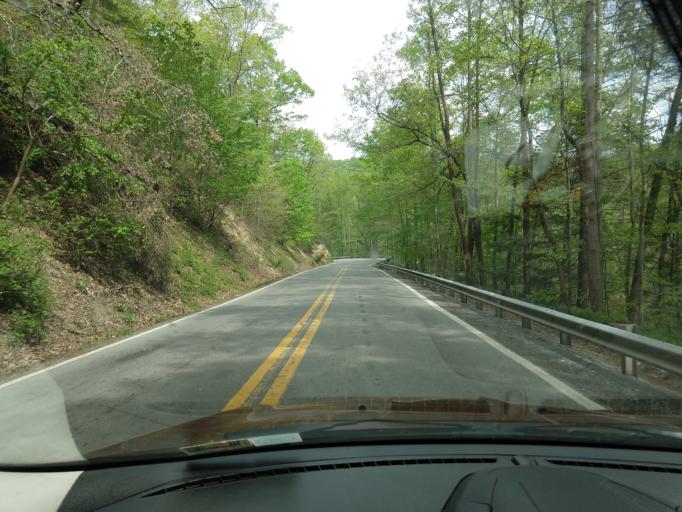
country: US
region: West Virginia
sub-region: McDowell County
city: Welch
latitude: 37.3618
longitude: -81.6481
